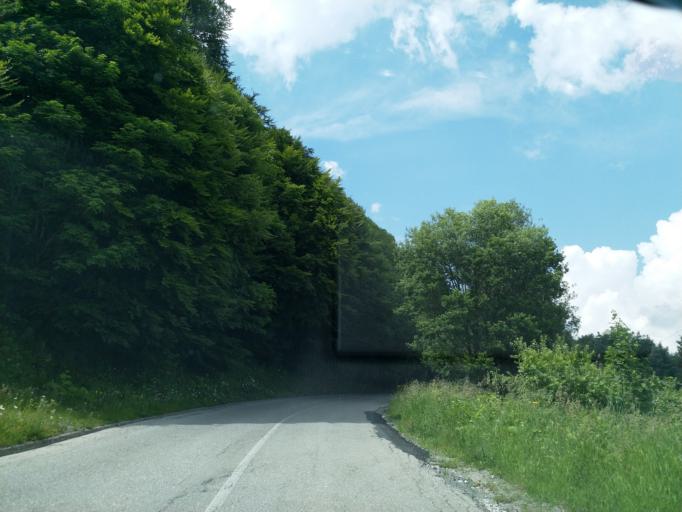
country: XK
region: Mitrovica
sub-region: Komuna e Leposaviqit
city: Leposaviq
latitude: 43.3155
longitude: 20.8494
